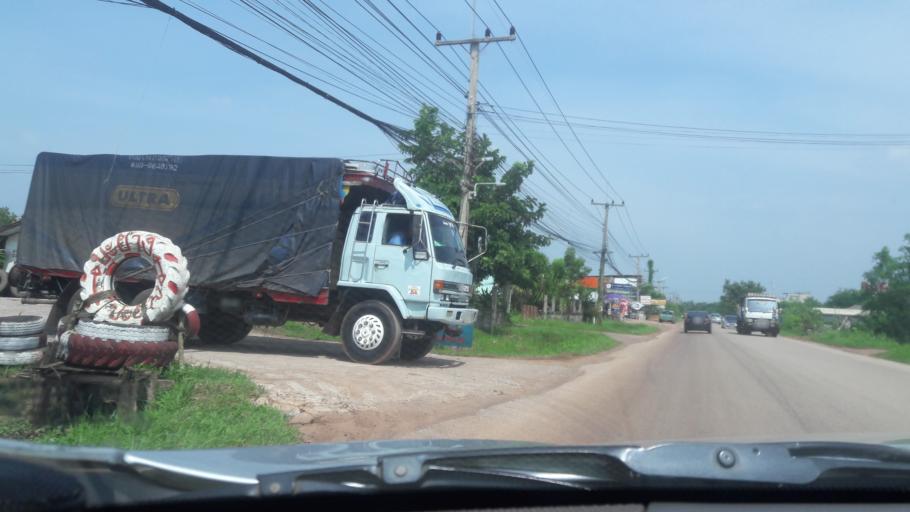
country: TH
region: Changwat Udon Thani
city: Udon Thani
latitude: 17.4323
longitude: 102.8269
